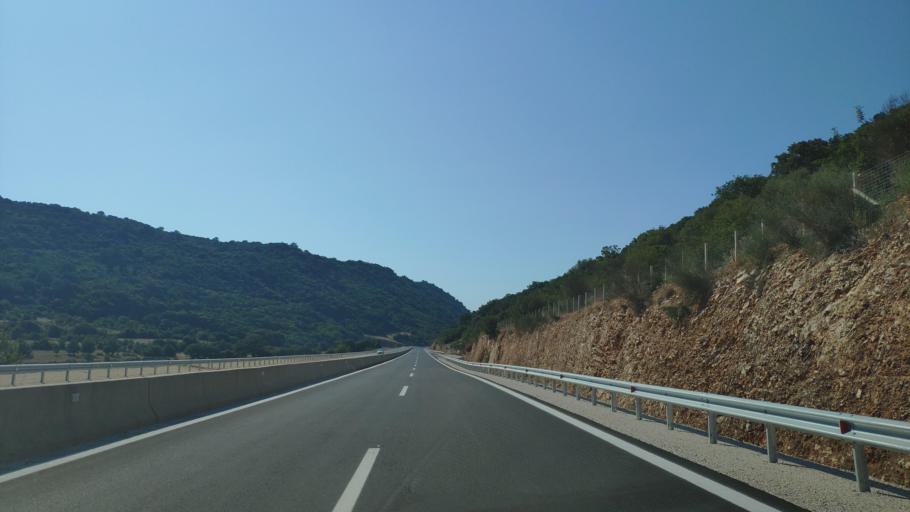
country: GR
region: West Greece
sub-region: Nomos Aitolias kai Akarnanias
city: Katouna
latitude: 38.8480
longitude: 21.0973
